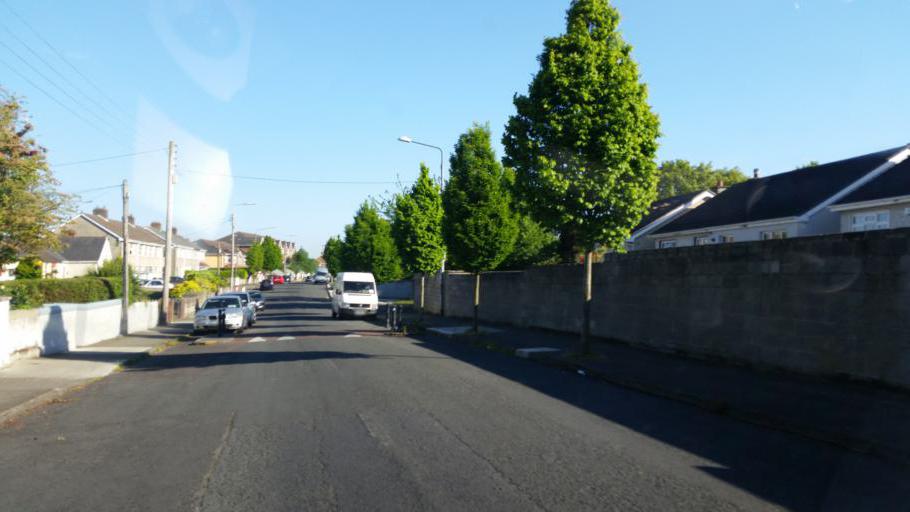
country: IE
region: Leinster
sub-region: Dublin City
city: Finglas
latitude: 53.3942
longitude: -6.3032
